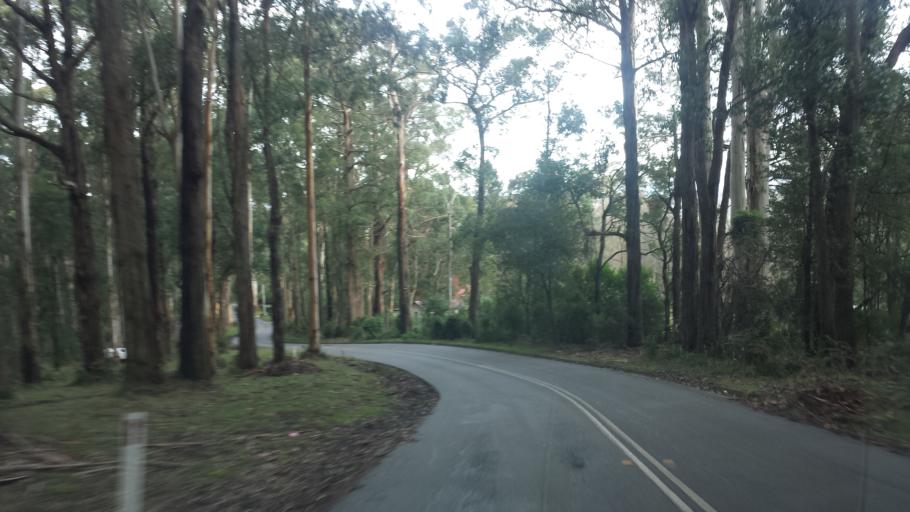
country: AU
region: Victoria
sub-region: Yarra Ranges
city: Belgrave
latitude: -37.8910
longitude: 145.3460
